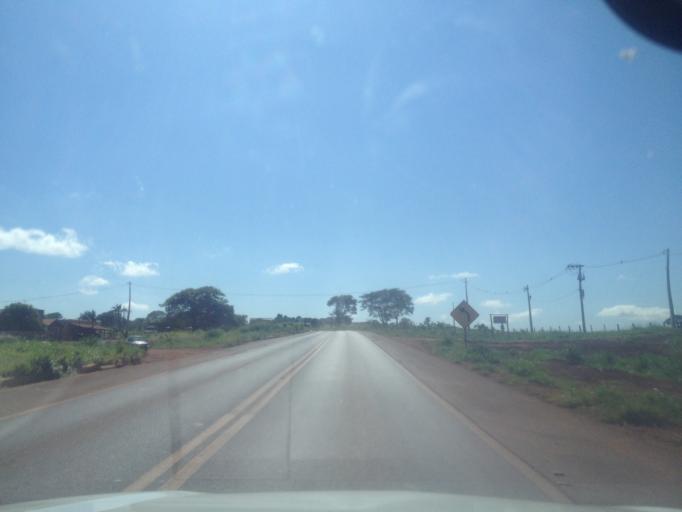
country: BR
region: Minas Gerais
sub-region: Santa Vitoria
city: Santa Vitoria
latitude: -19.0467
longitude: -50.4917
